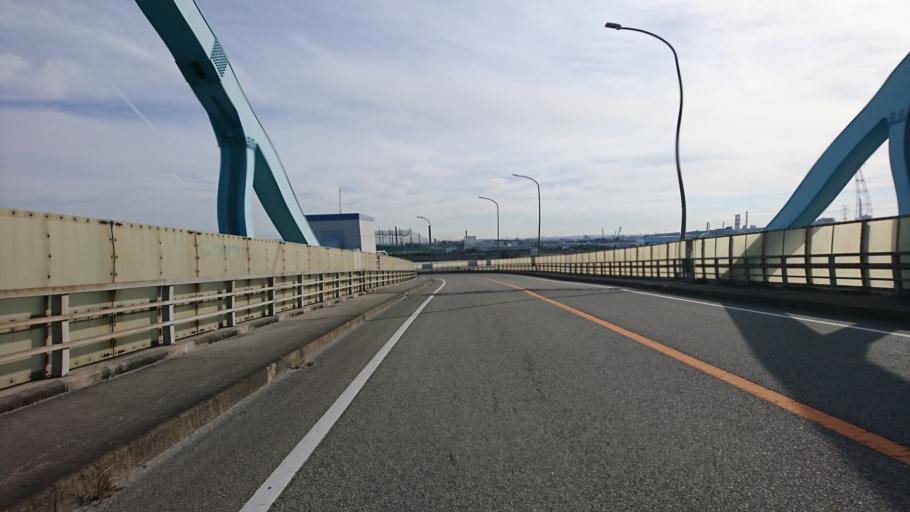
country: JP
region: Hyogo
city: Kakogawacho-honmachi
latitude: 34.7403
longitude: 134.8044
